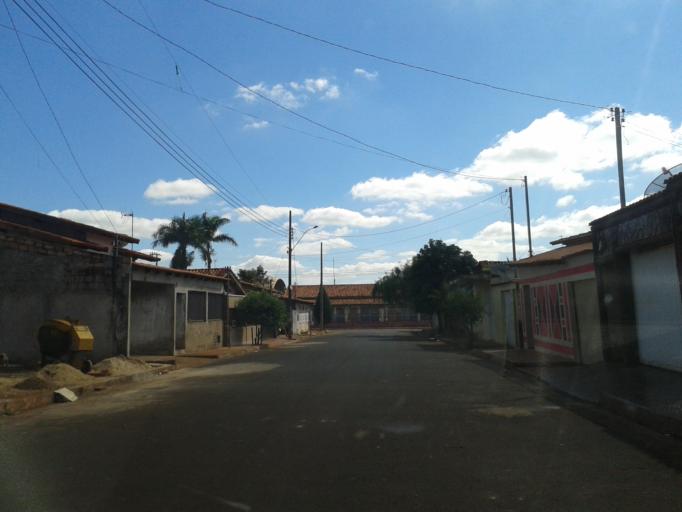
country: BR
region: Minas Gerais
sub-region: Centralina
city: Centralina
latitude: -18.5818
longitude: -49.2030
